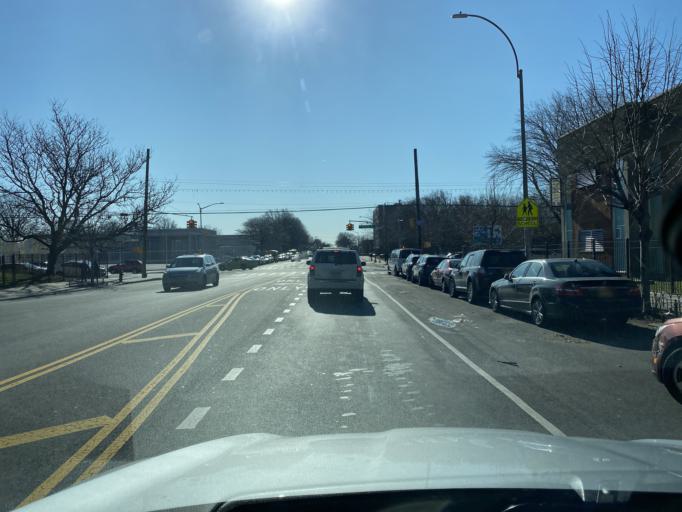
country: US
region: New York
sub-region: Bronx
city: The Bronx
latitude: 40.8204
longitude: -73.8581
